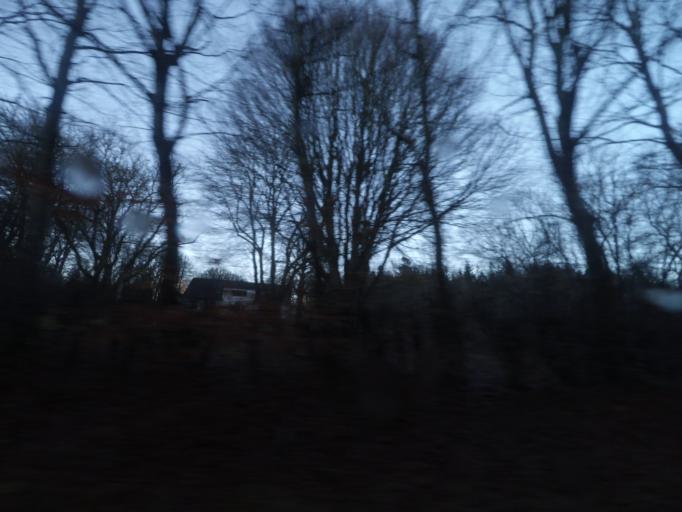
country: DK
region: Central Jutland
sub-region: Ikast-Brande Kommune
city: Brande
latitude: 56.0089
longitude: 9.0726
